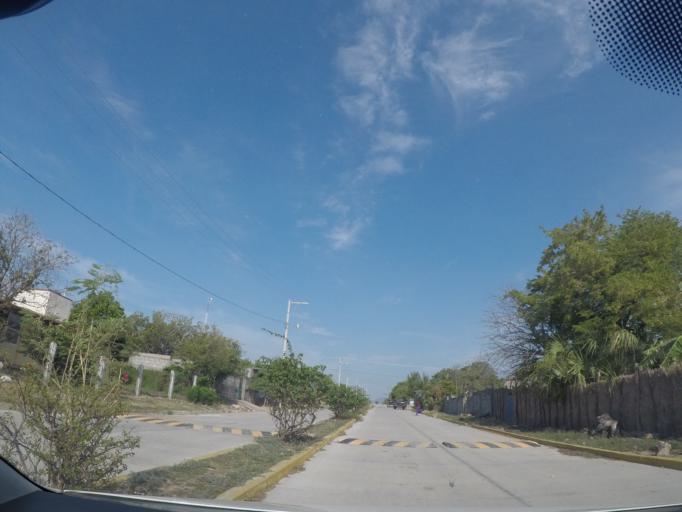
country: MX
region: Oaxaca
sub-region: Salina Cruz
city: Salina Cruz
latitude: 16.2199
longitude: -95.1262
